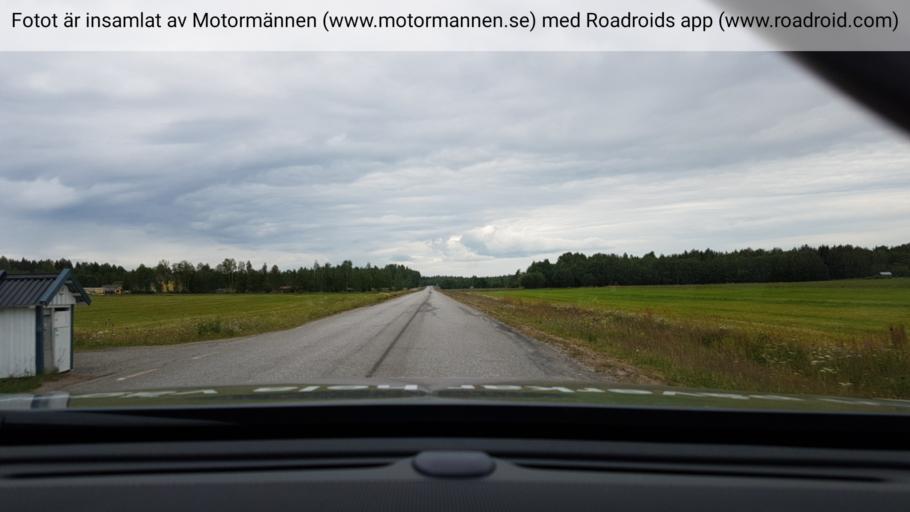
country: SE
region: Vaesterbotten
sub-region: Vannas Kommun
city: Vannasby
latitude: 64.0484
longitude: 19.9354
